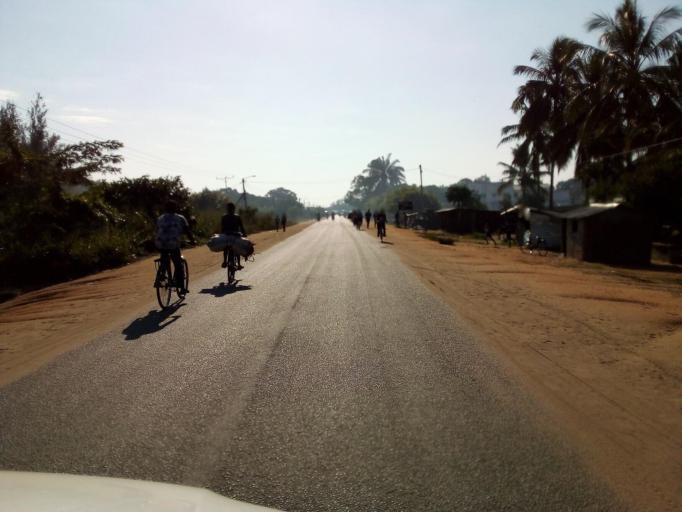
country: MZ
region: Zambezia
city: Quelimane
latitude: -17.5981
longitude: 36.8092
